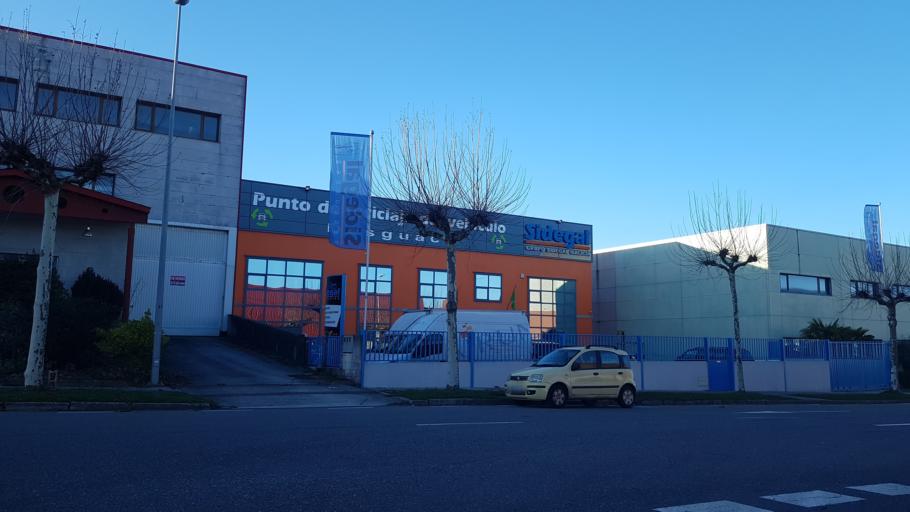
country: ES
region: Galicia
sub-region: Provincia de Lugo
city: Lugo
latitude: 43.0473
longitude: -7.5633
